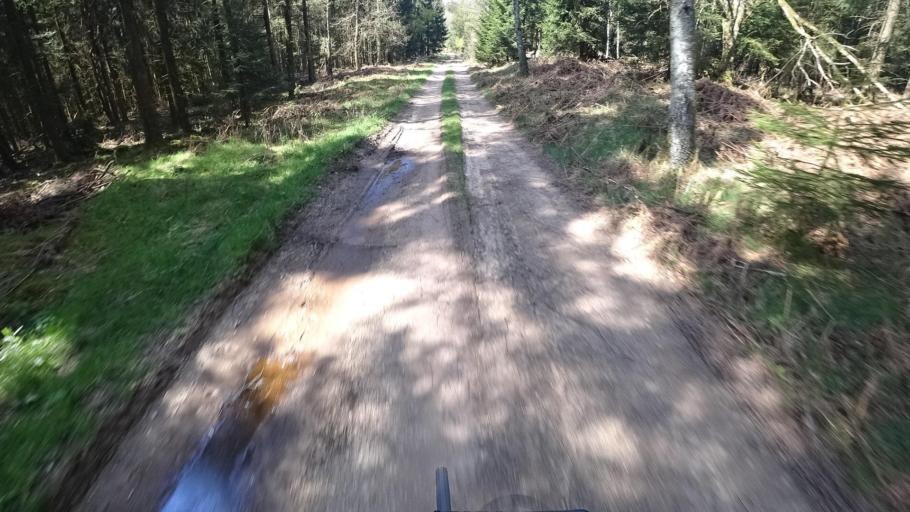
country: DE
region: Rheinland-Pfalz
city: Gusenburg
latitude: 49.6490
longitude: 6.9119
